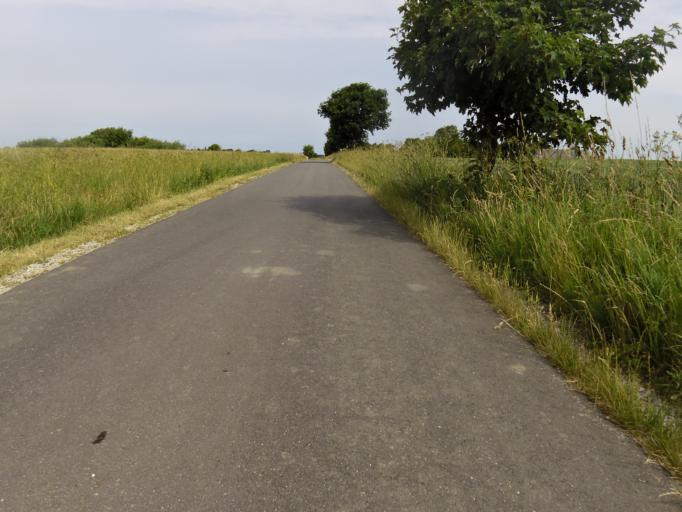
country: DK
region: Central Jutland
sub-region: Holstebro Kommune
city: Holstebro
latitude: 56.4314
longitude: 8.6690
